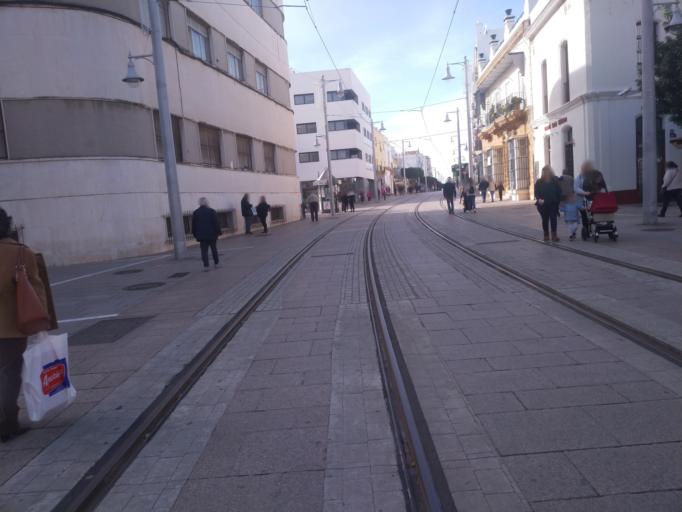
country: ES
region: Andalusia
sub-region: Provincia de Cadiz
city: San Fernando
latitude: 36.4581
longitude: -6.2038
